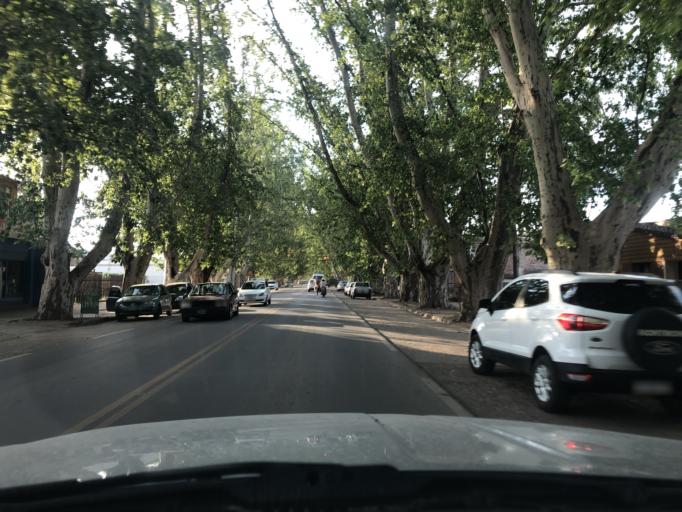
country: AR
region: Cordoba
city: Jesus Maria
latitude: -31.0097
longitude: -64.0753
